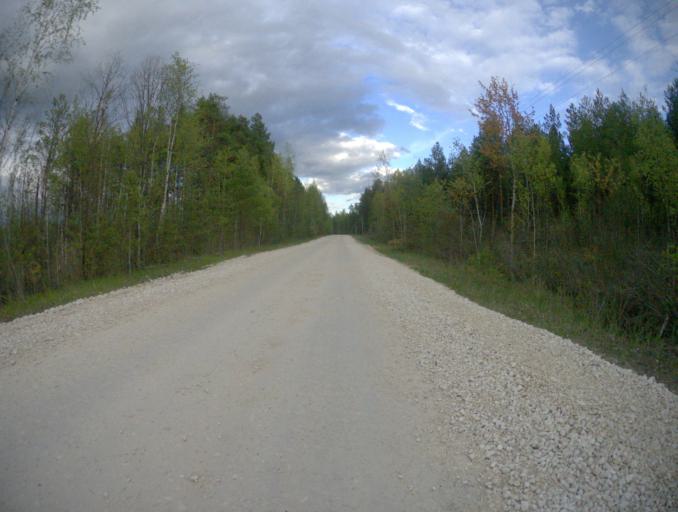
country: RU
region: Vladimir
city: Anopino
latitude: 55.7193
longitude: 40.6021
